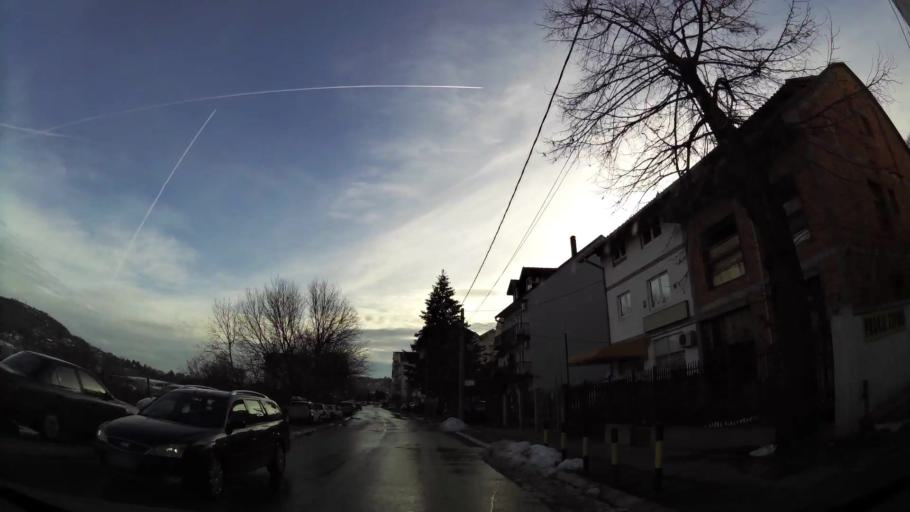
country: RS
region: Central Serbia
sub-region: Belgrade
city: Rakovica
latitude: 44.7401
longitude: 20.4314
